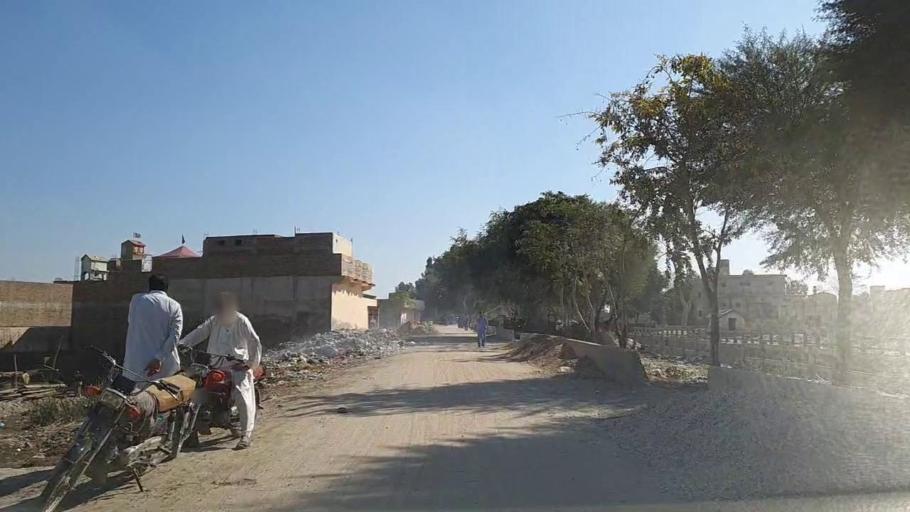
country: PK
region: Sindh
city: Nawabshah
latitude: 26.2549
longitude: 68.4188
